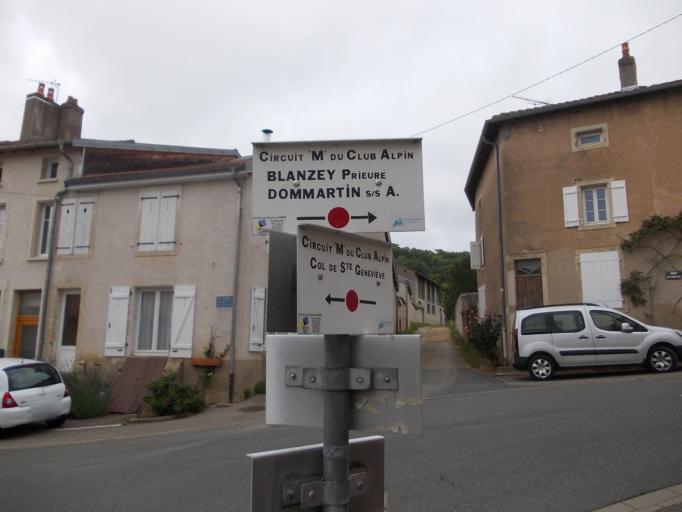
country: FR
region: Lorraine
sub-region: Departement de Meurthe-et-Moselle
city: Eulmont
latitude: 48.7503
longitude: 6.2235
